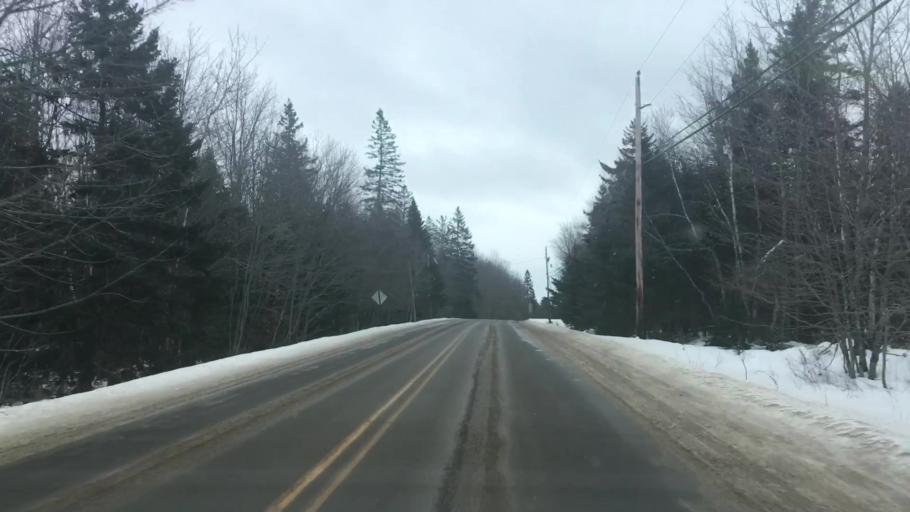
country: US
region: Maine
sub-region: Washington County
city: East Machias
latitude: 44.9853
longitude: -67.4571
